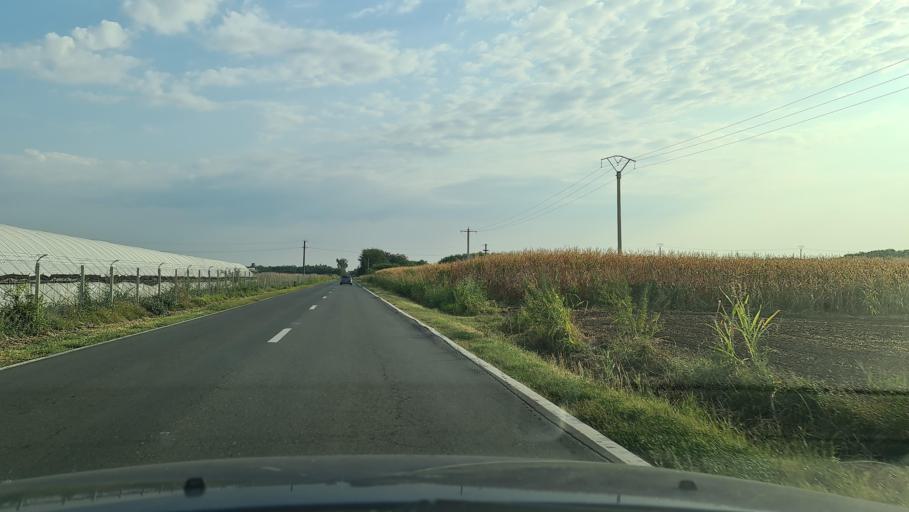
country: RO
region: Calarasi
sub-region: Comuna Dor Marunt
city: Dor Marunt
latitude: 44.4489
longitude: 26.8969
